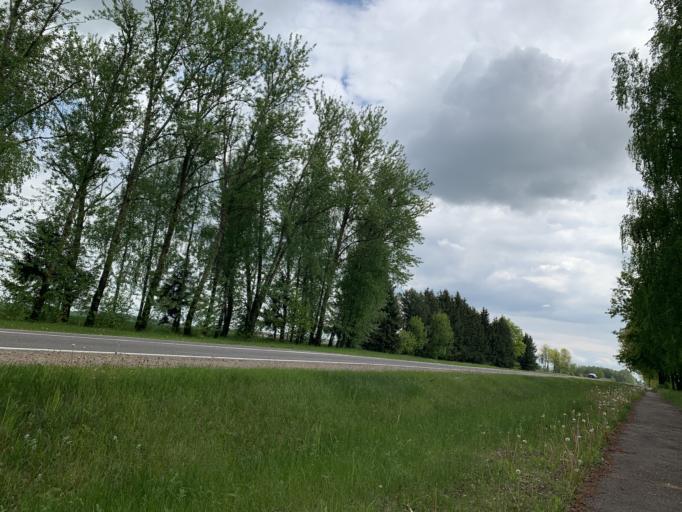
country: BY
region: Minsk
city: Nyasvizh
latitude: 53.2449
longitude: 26.6762
